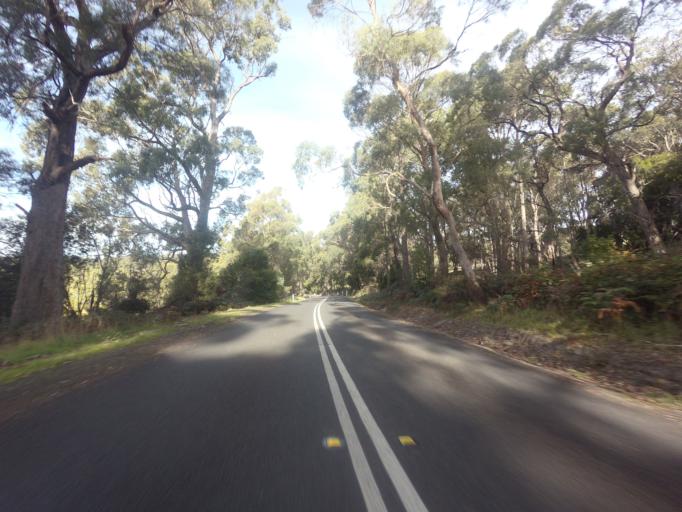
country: AU
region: Tasmania
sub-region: Clarence
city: Sandford
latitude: -43.0538
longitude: 147.7908
